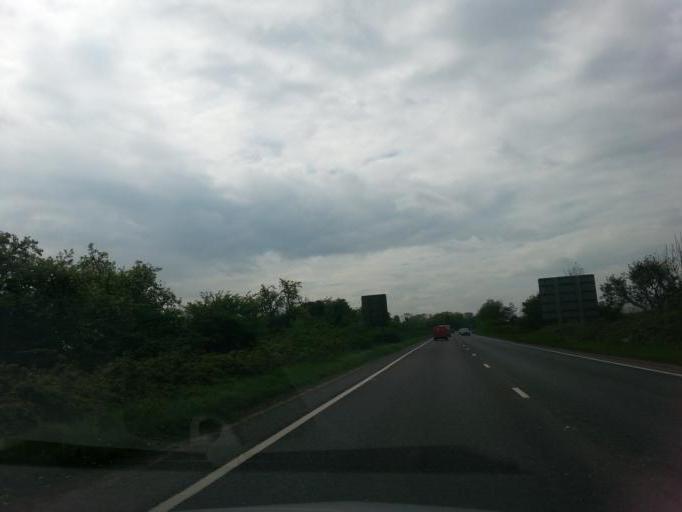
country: GB
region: England
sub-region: Cambridgeshire
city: Wisbech
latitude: 52.6474
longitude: 0.1700
